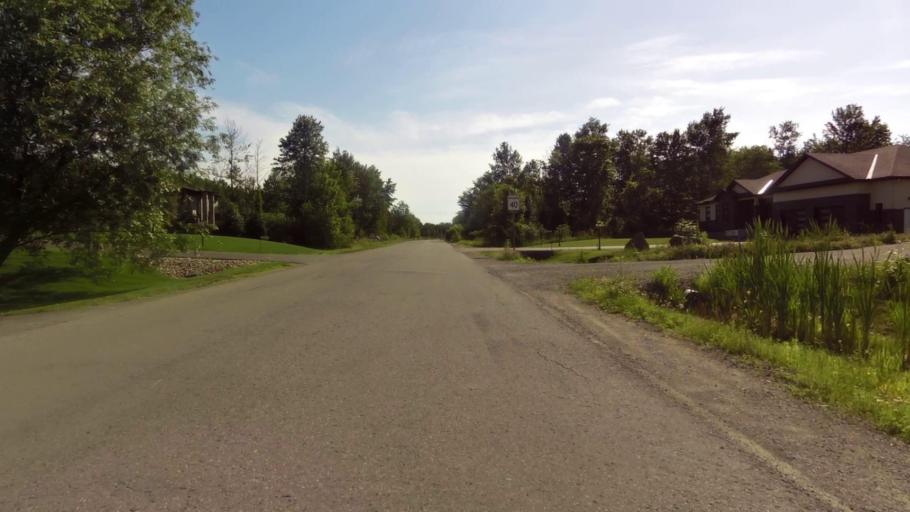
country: CA
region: Ontario
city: Ottawa
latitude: 45.2620
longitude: -75.5906
